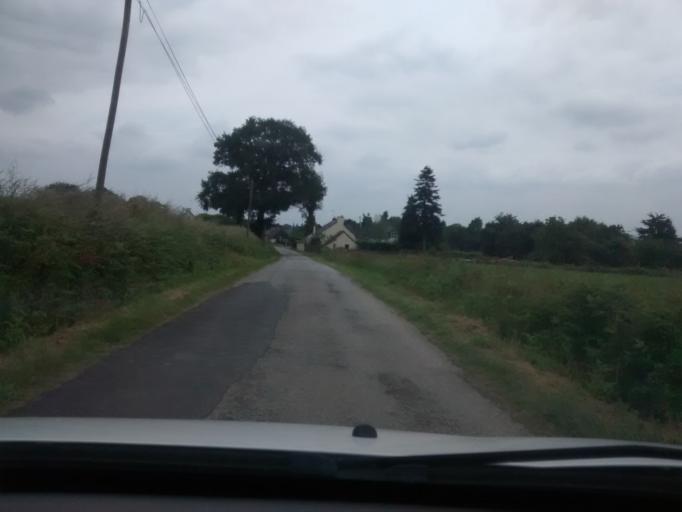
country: FR
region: Brittany
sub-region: Departement d'Ille-et-Vilaine
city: Servon-sur-Vilaine
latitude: 48.1303
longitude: -1.4619
